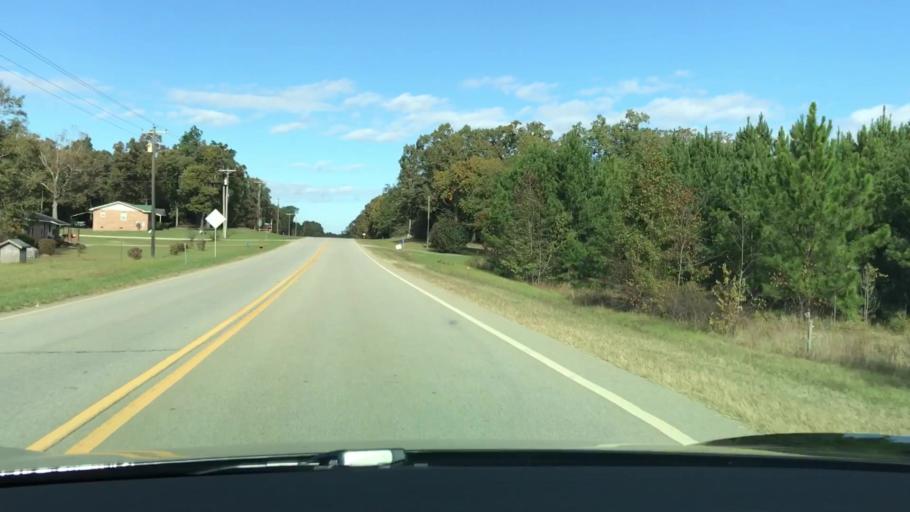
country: US
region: Georgia
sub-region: Jefferson County
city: Wrens
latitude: 33.1890
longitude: -82.4564
